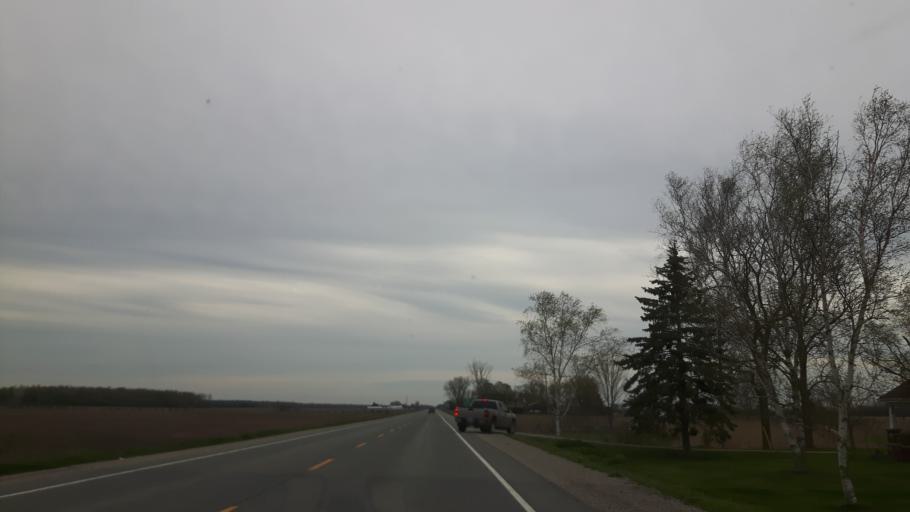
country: CA
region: Ontario
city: Goderich
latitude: 43.6472
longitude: -81.7059
